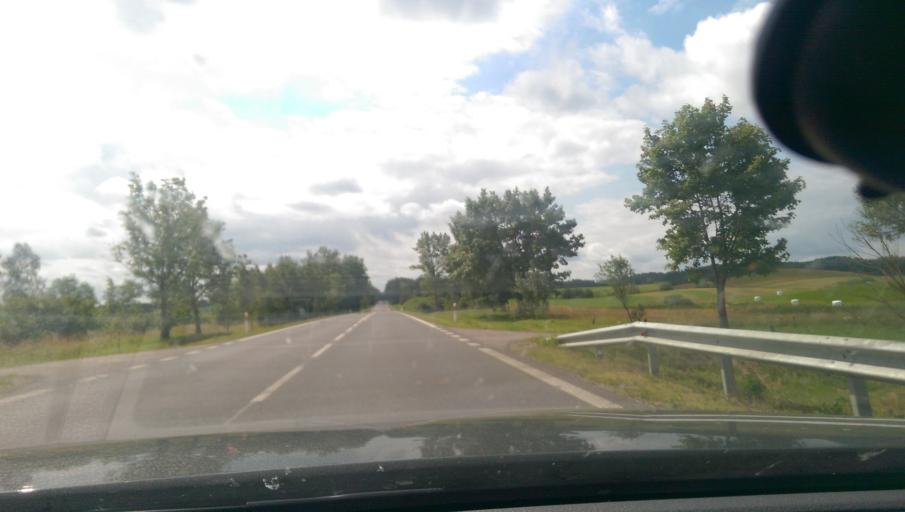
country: PL
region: Warmian-Masurian Voivodeship
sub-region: Powiat olecki
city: Kowale Oleckie
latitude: 54.1984
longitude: 22.4111
